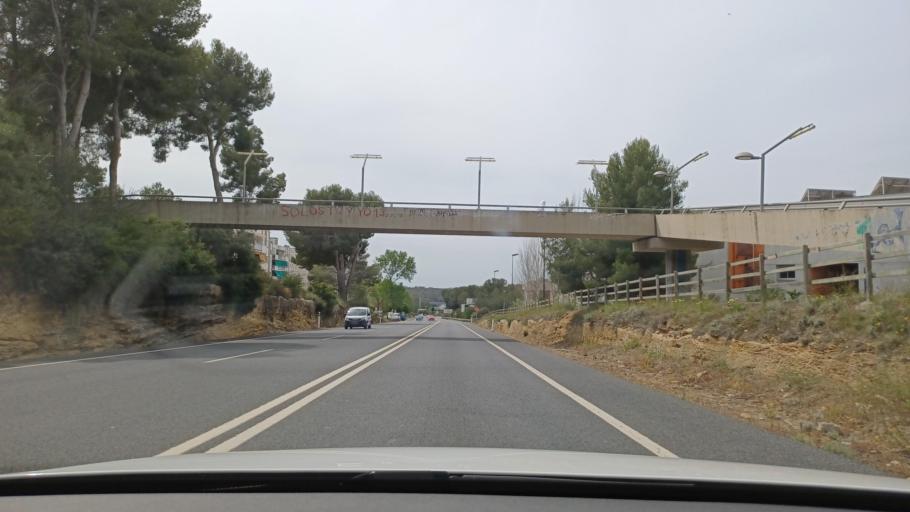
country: ES
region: Catalonia
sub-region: Provincia de Tarragona
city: Constanti
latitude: 41.1571
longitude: 1.2401
